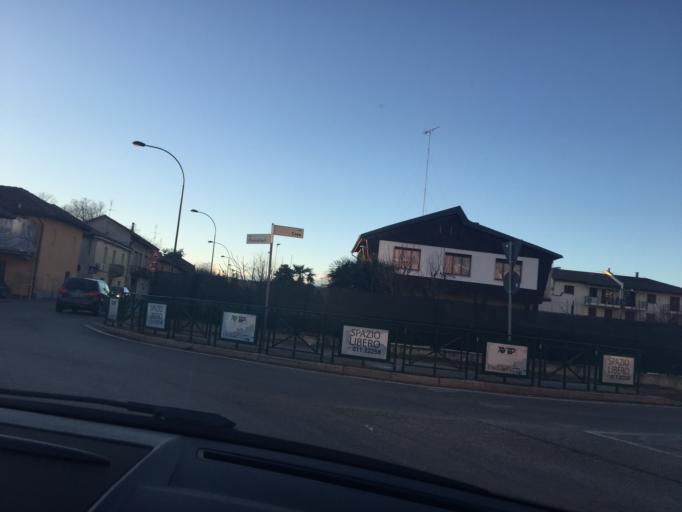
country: IT
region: Piedmont
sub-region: Provincia di Torino
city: Gerbido
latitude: 45.0450
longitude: 7.6159
